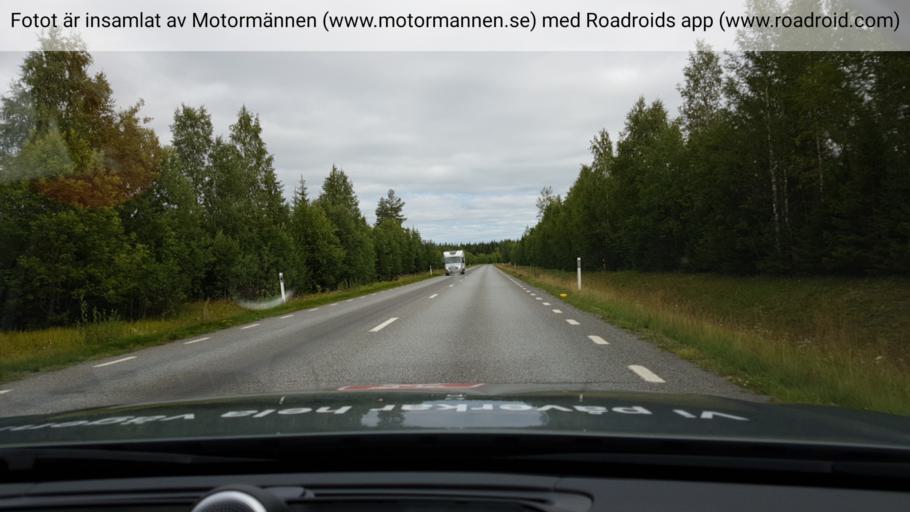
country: SE
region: Jaemtland
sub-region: Stroemsunds Kommun
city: Stroemsund
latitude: 63.5129
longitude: 15.2867
